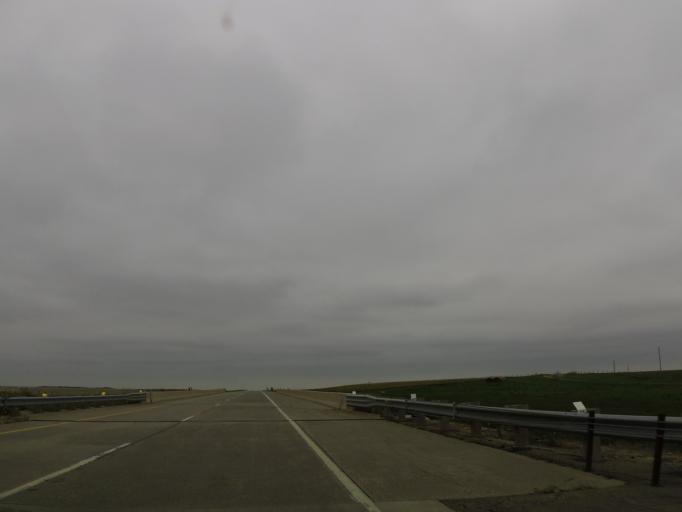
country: US
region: South Dakota
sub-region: Roberts County
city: Sisseton
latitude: 45.3834
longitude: -97.0420
